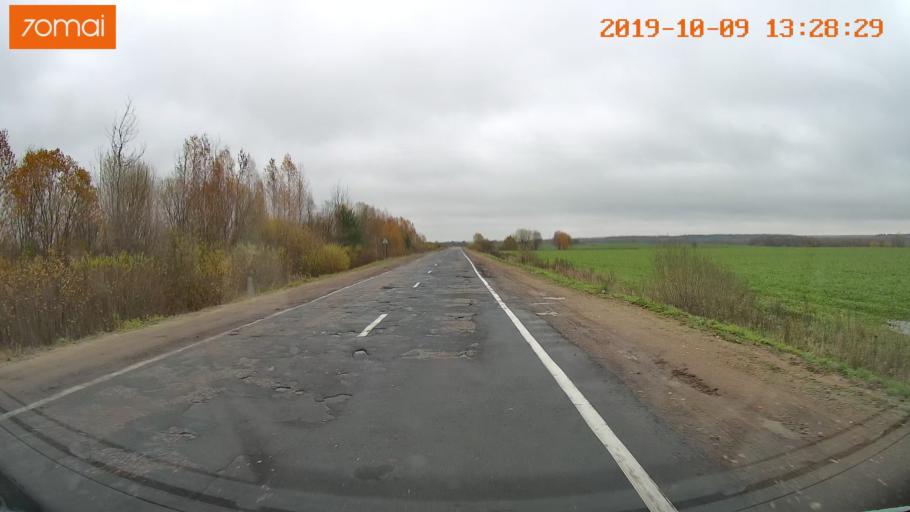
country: RU
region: Jaroslavl
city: Lyubim
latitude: 58.3142
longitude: 40.9697
